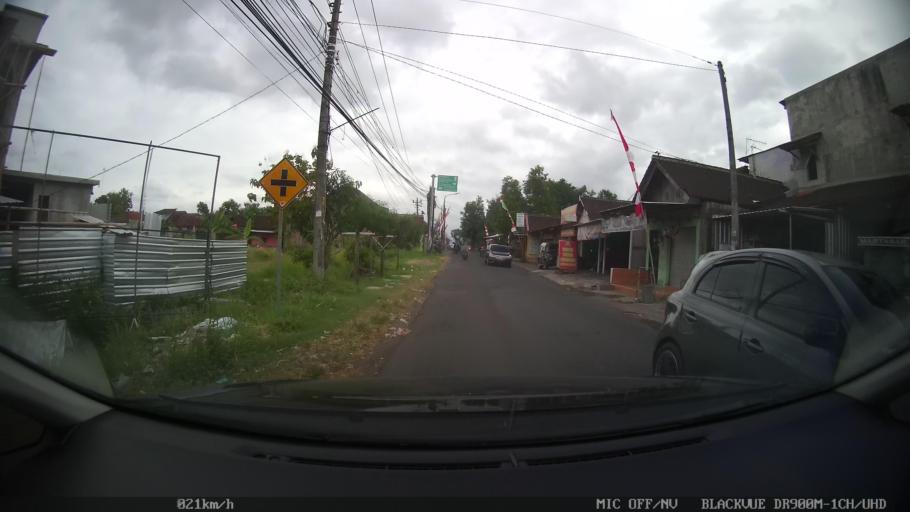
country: ID
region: Daerah Istimewa Yogyakarta
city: Sewon
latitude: -7.8394
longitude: 110.4115
